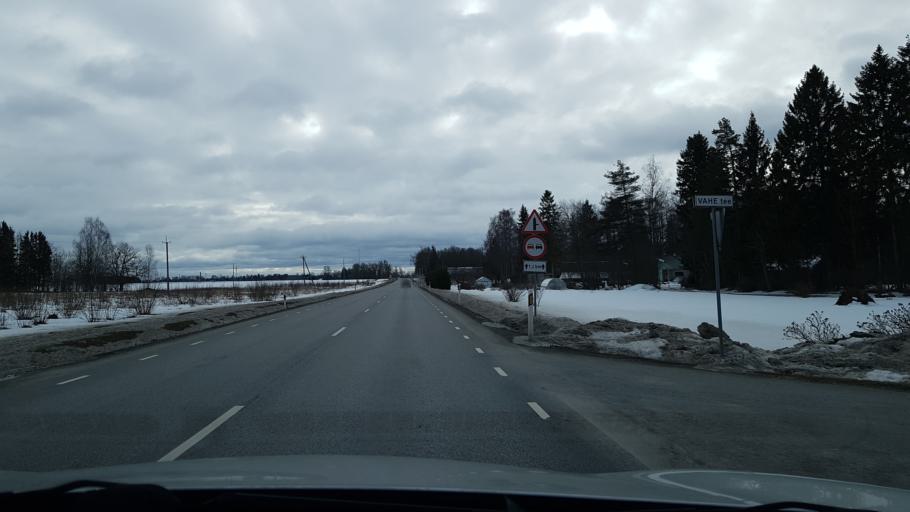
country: EE
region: Jogevamaa
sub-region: Jogeva linn
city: Jogeva
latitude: 58.7656
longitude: 26.3312
